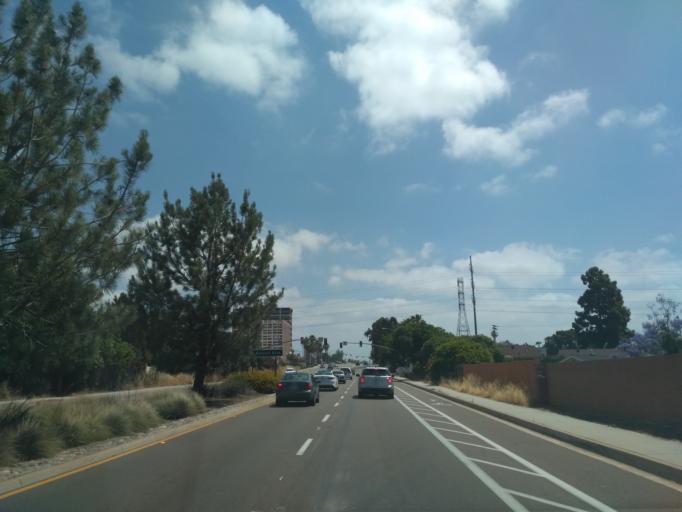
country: US
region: California
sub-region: San Diego County
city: La Jolla
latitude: 32.8175
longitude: -117.1868
